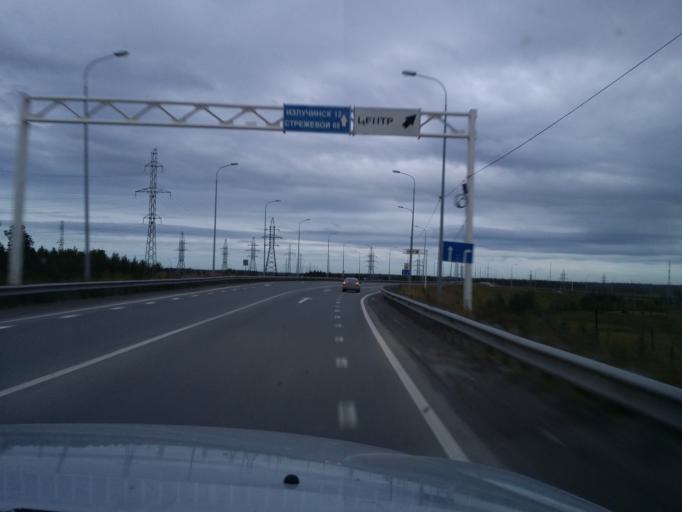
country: RU
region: Khanty-Mansiyskiy Avtonomnyy Okrug
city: Nizhnevartovsk
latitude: 60.9510
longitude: 76.6633
